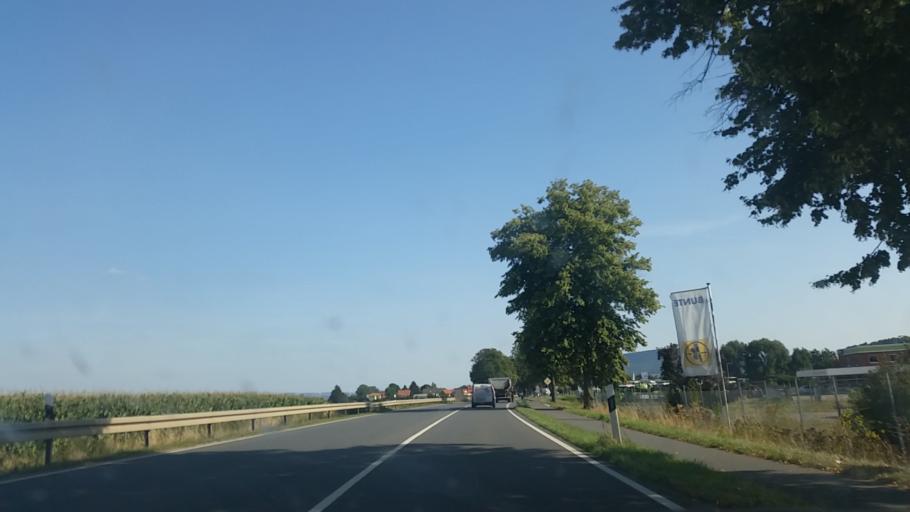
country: DE
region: Lower Saxony
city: Coppenbrugge
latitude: 52.1150
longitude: 9.5582
